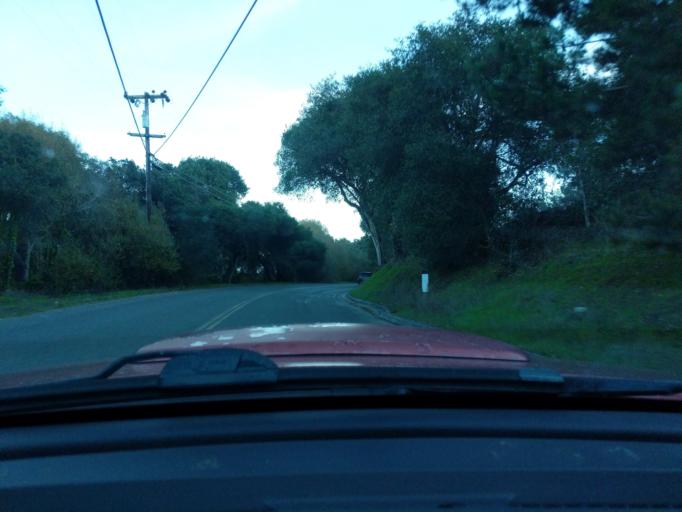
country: US
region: California
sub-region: San Benito County
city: Aromas
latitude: 36.8532
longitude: -121.6810
